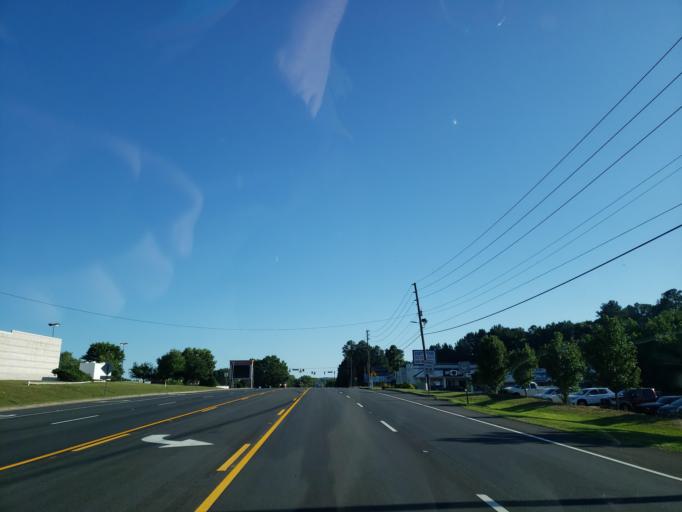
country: US
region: Georgia
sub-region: Floyd County
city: Rome
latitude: 34.3040
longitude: -85.1750
